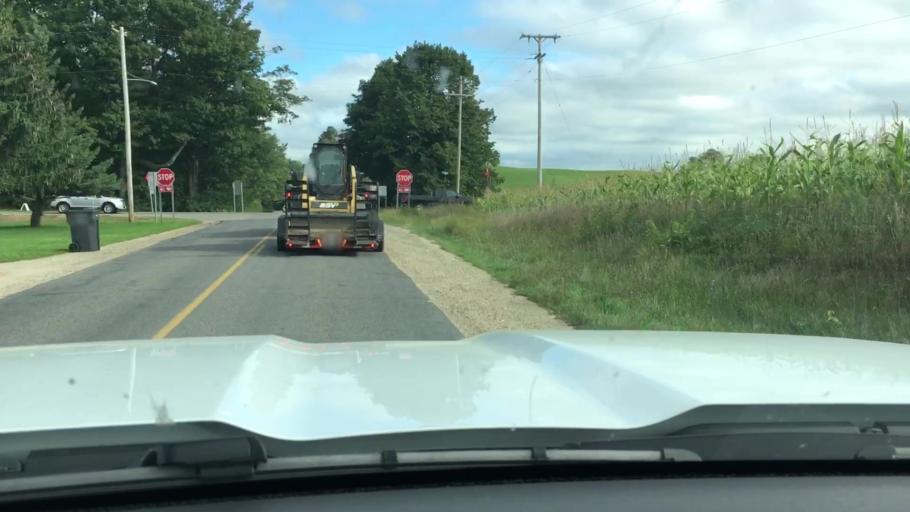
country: US
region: Michigan
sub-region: Kent County
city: Byron Center
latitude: 42.8110
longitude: -85.8026
